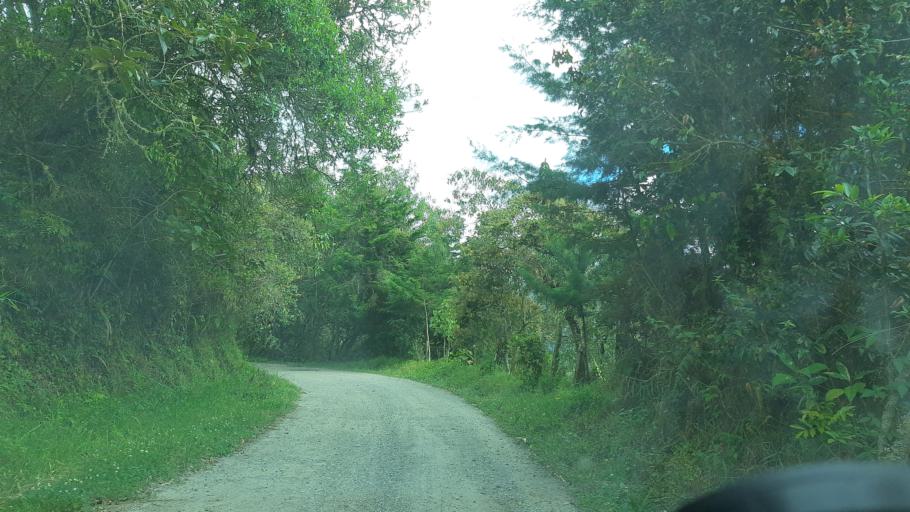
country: CO
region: Boyaca
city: Garagoa
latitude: 5.0471
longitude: -73.3497
